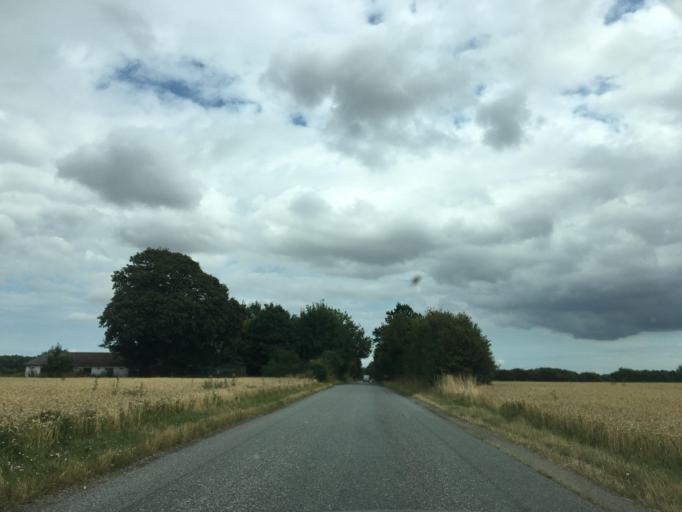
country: DK
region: South Denmark
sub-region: Kerteminde Kommune
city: Langeskov
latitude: 55.3198
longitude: 10.5920
